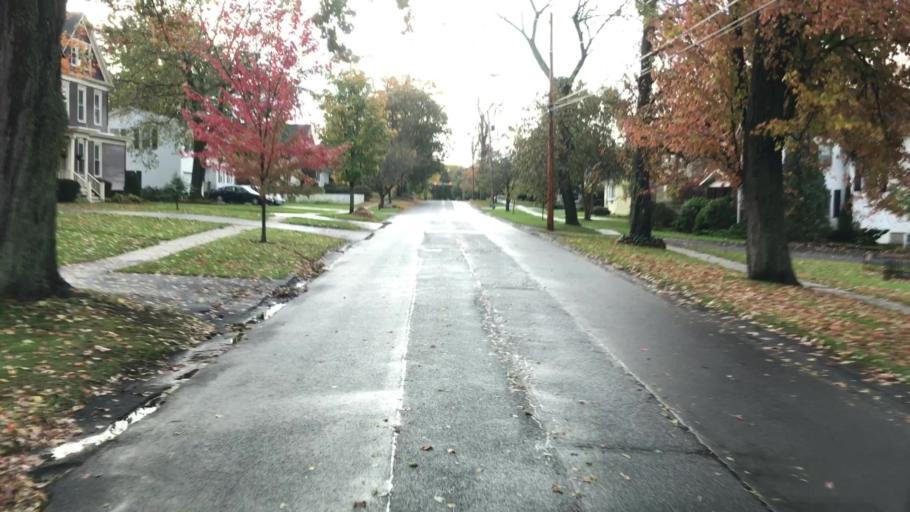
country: US
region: New York
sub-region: Onondaga County
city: Skaneateles
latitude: 42.9462
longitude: -76.4169
